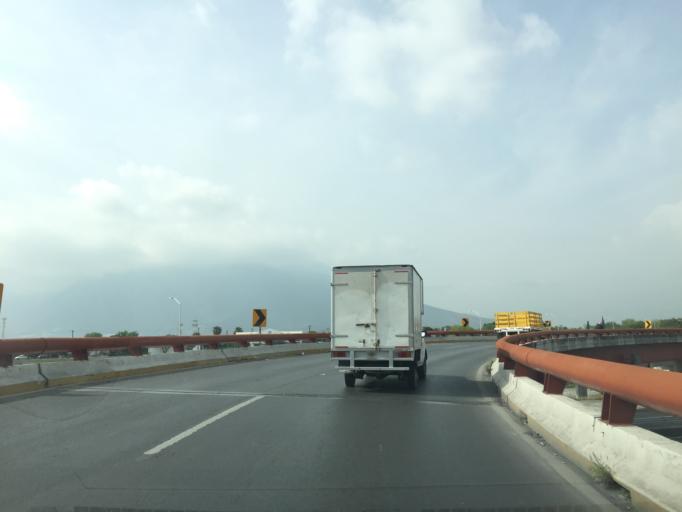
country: MX
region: Nuevo Leon
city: Guadalupe
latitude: 25.6905
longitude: -100.2388
